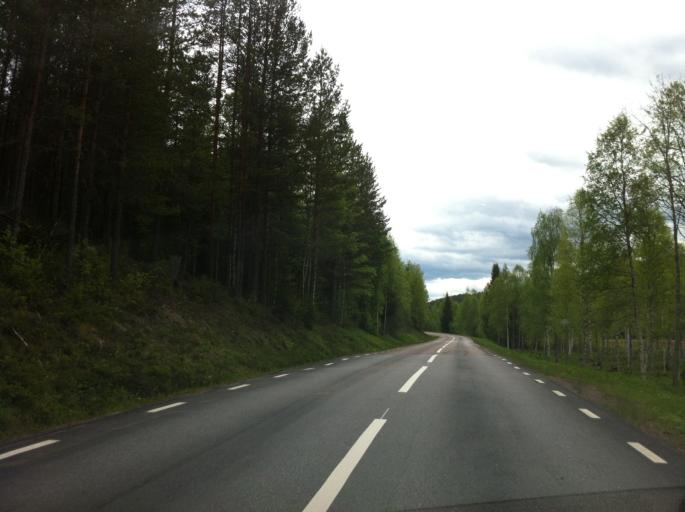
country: SE
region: Dalarna
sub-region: Malung-Saelens kommun
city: Malung
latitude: 61.2885
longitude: 13.1591
